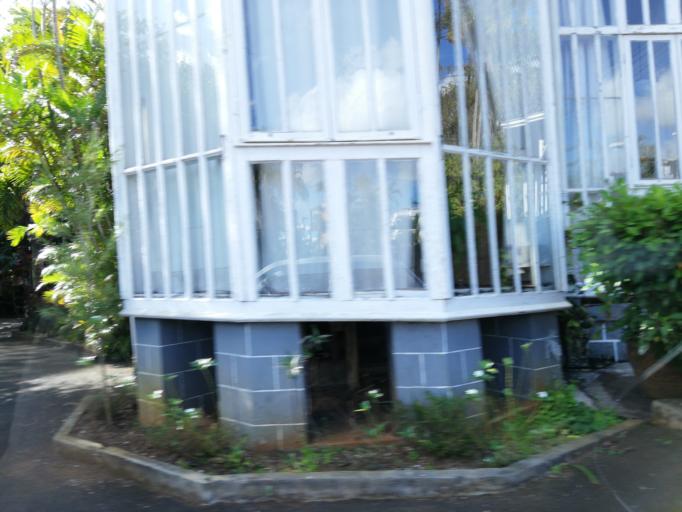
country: MU
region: Moka
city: Moka
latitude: -20.2256
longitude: 57.4702
